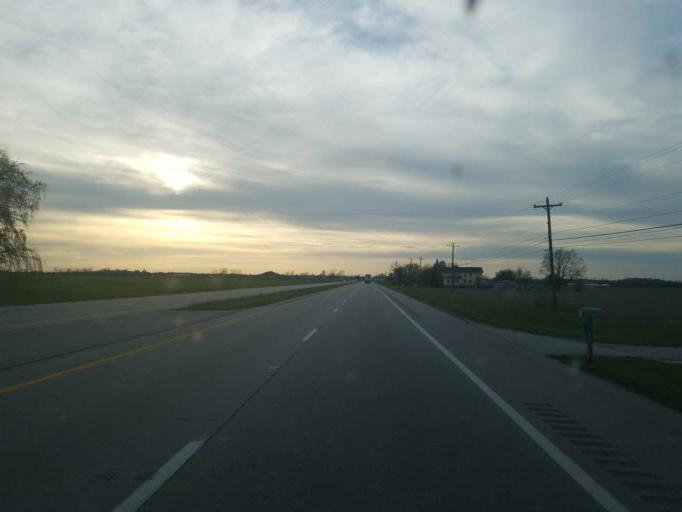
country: US
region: Ohio
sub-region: Sandusky County
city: Woodville
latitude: 41.4390
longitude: -83.3345
